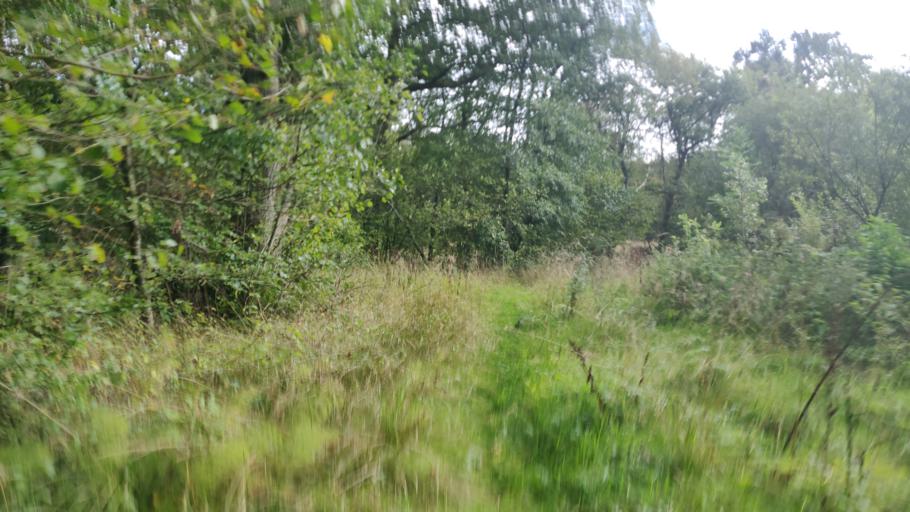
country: DK
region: South Denmark
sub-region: Kolding Kommune
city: Lunderskov
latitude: 55.5458
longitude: 9.3640
